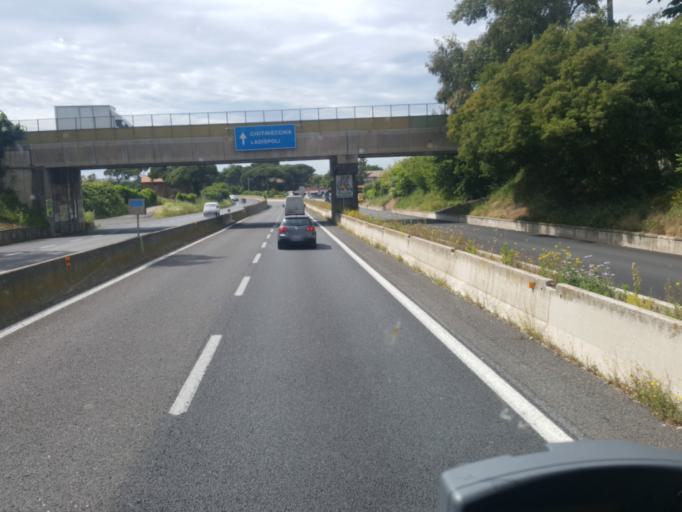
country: IT
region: Latium
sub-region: Citta metropolitana di Roma Capitale
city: Ara Nova
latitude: 41.9181
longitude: 12.2381
